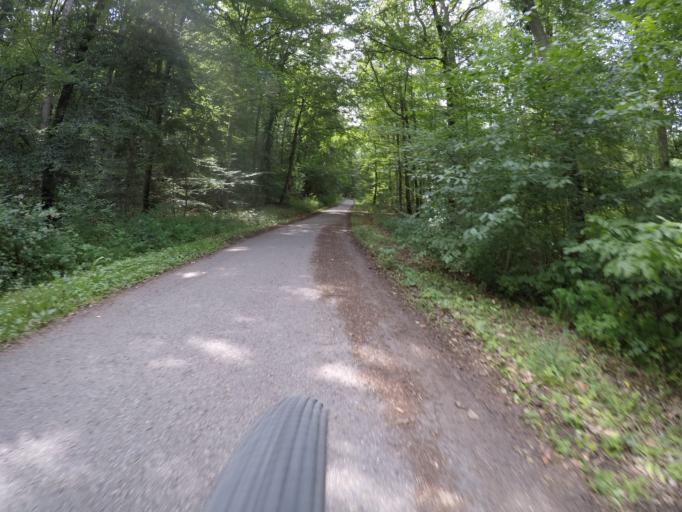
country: DE
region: Baden-Wuerttemberg
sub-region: Regierungsbezirk Stuttgart
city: Magstadt
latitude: 48.7371
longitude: 8.9979
